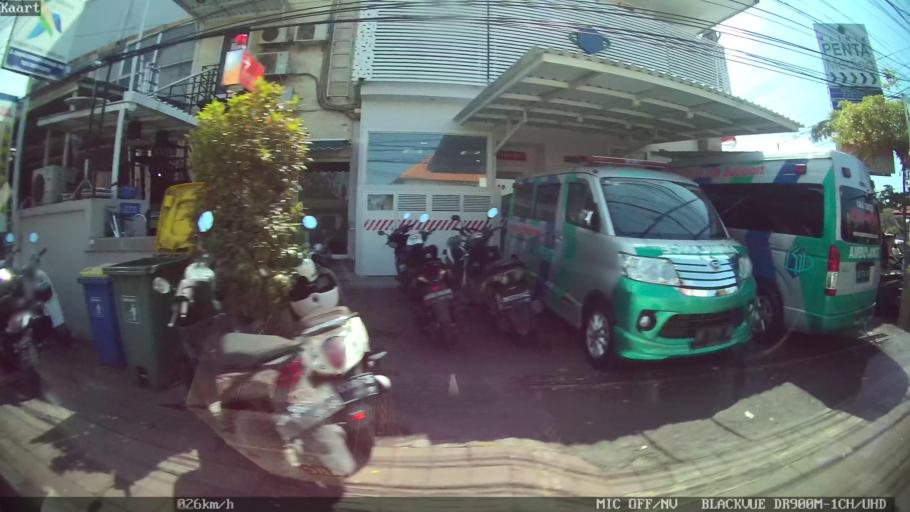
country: ID
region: Bali
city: Karyadharma
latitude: -8.6867
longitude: 115.1858
